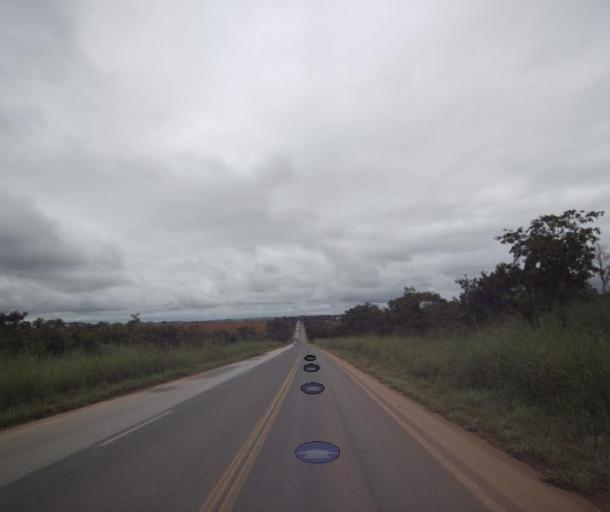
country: BR
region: Goias
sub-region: Uruacu
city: Uruacu
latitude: -14.5771
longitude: -49.1586
